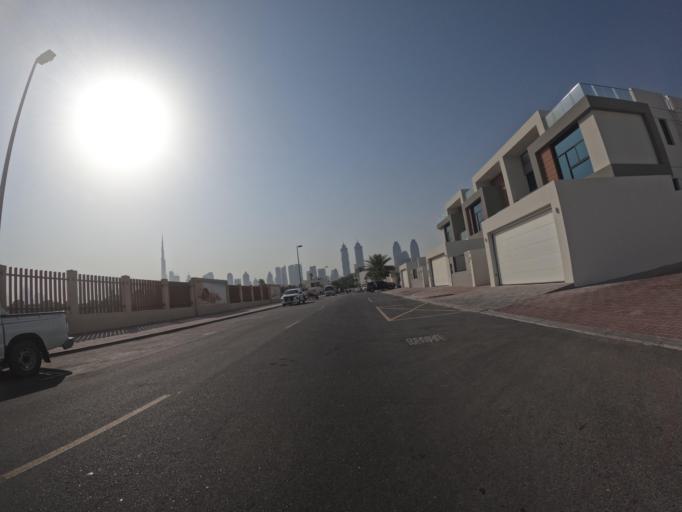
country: AE
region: Dubai
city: Dubai
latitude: 25.1952
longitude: 55.2411
